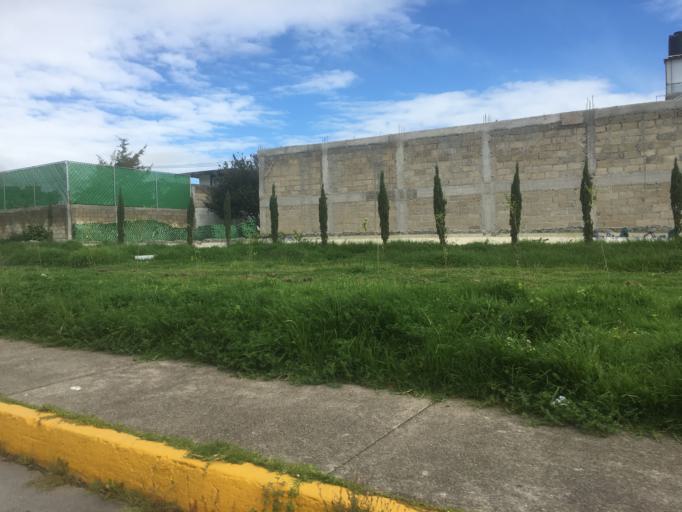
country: MX
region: Mexico
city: Santa Maria Totoltepec
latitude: 19.3029
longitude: -99.5906
